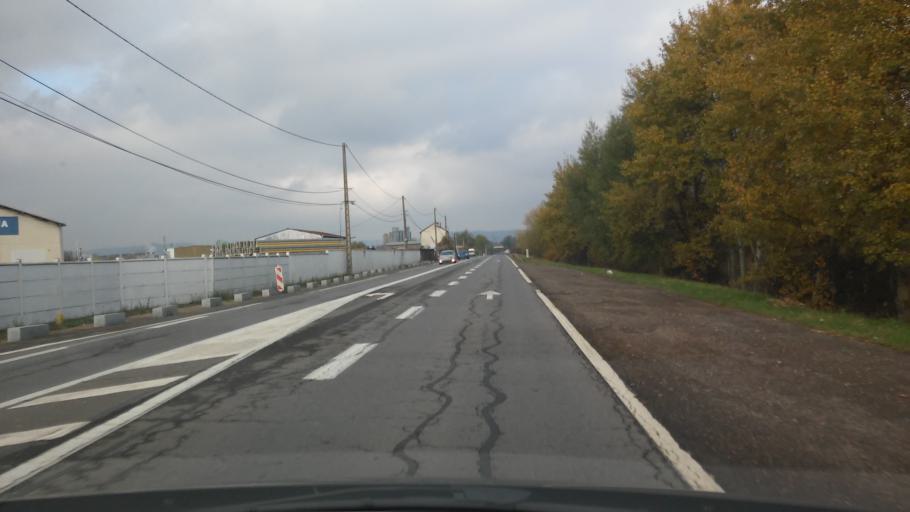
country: FR
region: Lorraine
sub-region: Departement de la Moselle
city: Uckange
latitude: 49.3190
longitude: 6.1558
